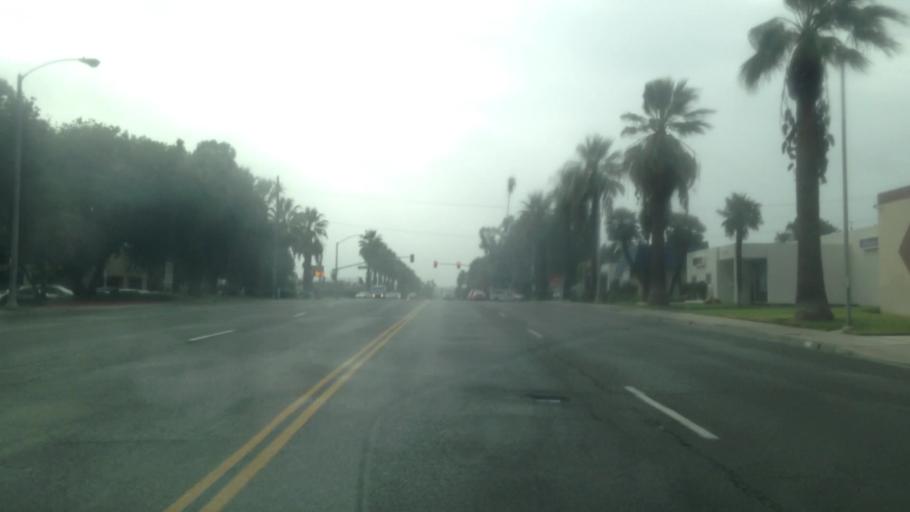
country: US
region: California
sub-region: Riverside County
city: Highgrove
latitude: 33.9846
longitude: -117.3485
